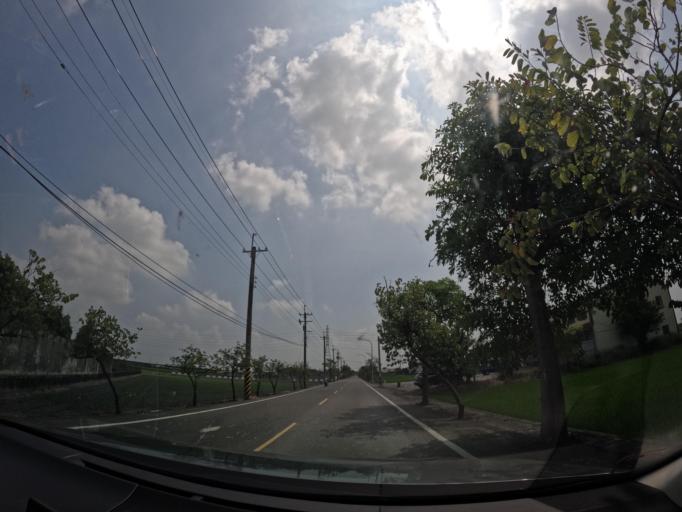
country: TW
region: Taiwan
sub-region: Yunlin
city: Douliu
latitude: 23.6729
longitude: 120.3971
